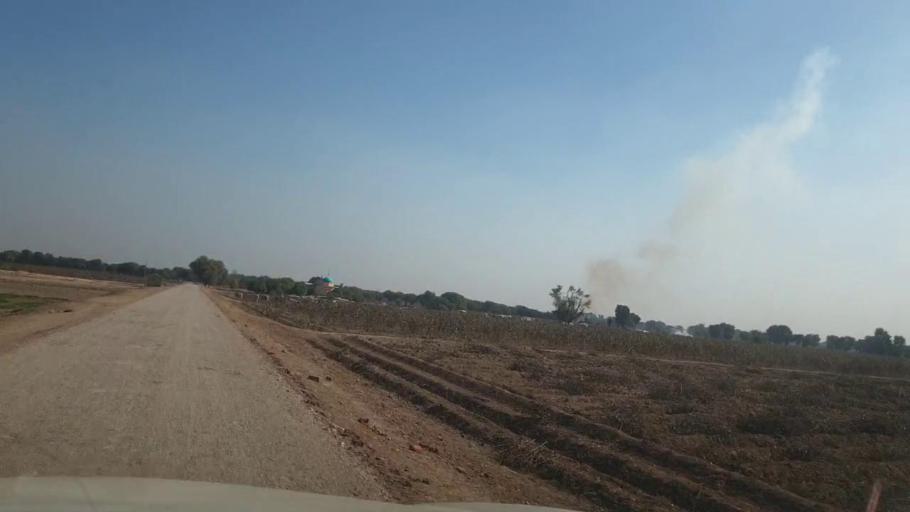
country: PK
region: Sindh
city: Bhan
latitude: 26.5793
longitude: 67.7025
